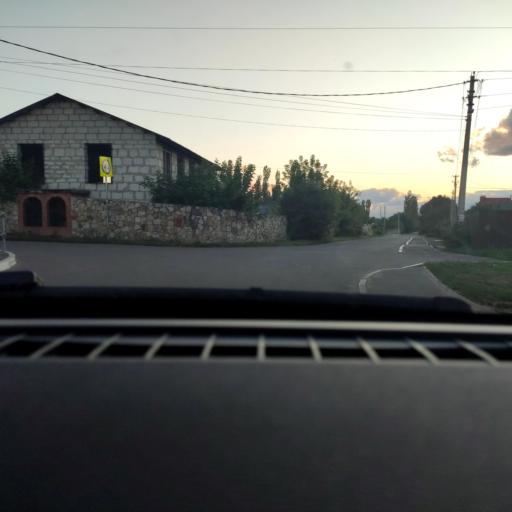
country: RU
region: Voronezj
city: Novaya Usman'
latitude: 51.6558
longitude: 39.3350
